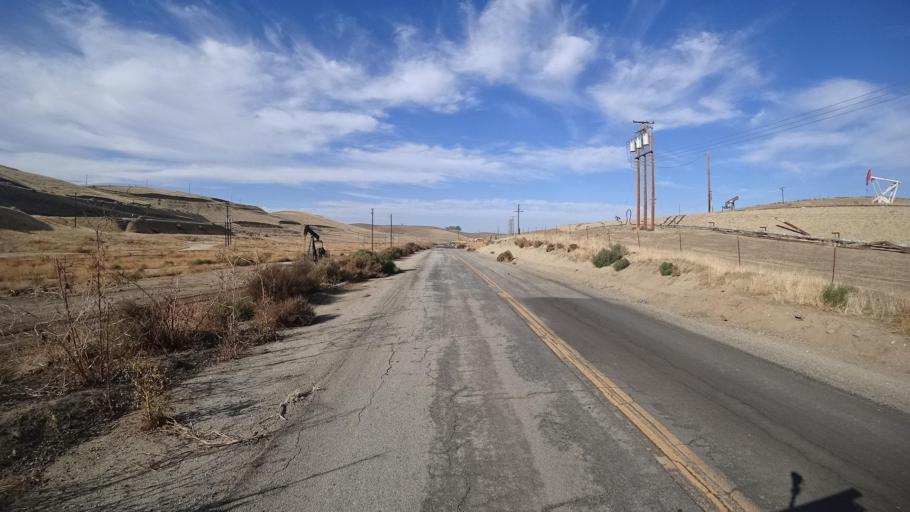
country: US
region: California
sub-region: Kern County
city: Oildale
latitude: 35.6120
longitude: -118.9745
